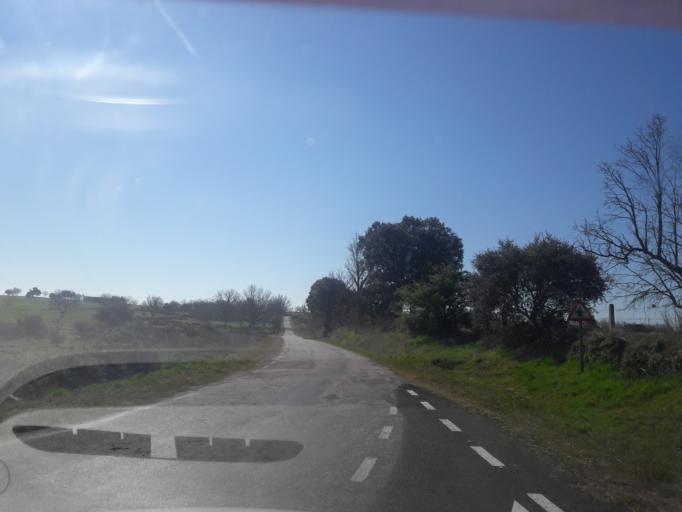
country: ES
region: Castille and Leon
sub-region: Provincia de Salamanca
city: Valsalabroso
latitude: 41.1721
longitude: -6.5065
